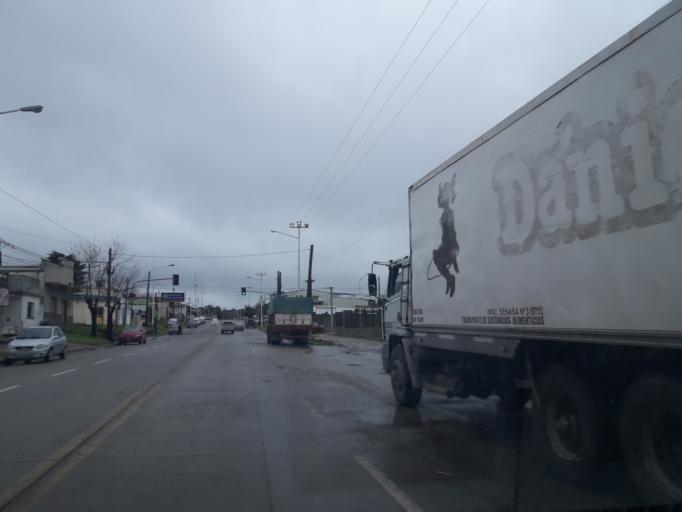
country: AR
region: Buenos Aires
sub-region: Partido de Tandil
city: Tandil
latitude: -37.3190
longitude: -59.1595
